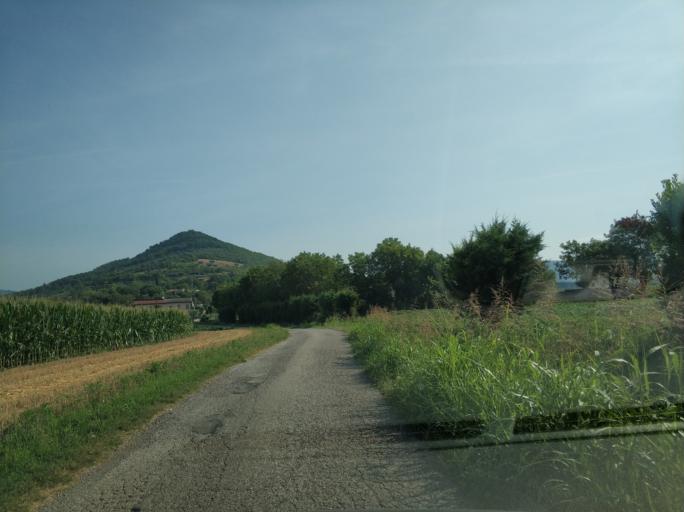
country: IT
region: Veneto
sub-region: Provincia di Padova
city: Baone
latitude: 45.2329
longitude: 11.6930
